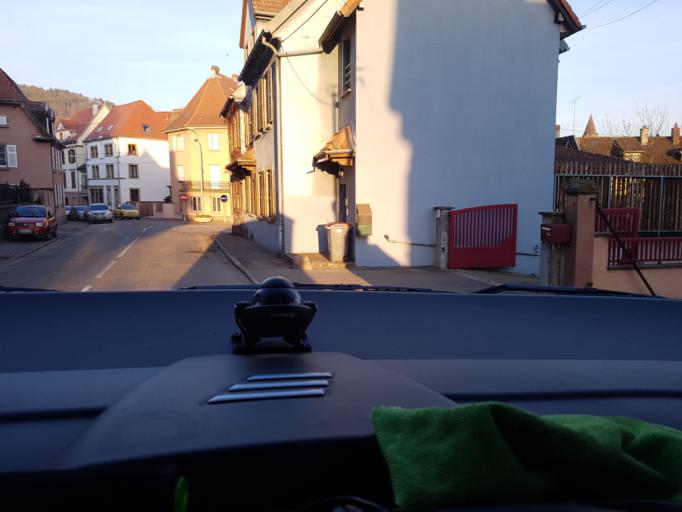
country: FR
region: Alsace
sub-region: Departement du Haut-Rhin
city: Munster
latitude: 48.0409
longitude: 7.1314
